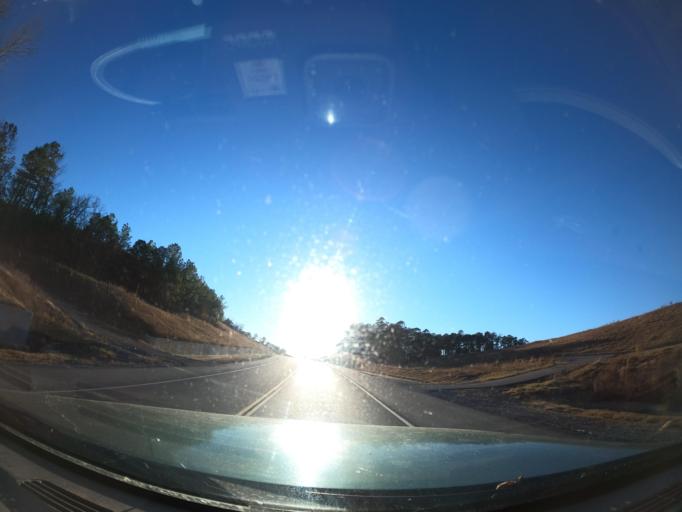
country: US
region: Oklahoma
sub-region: Pittsburg County
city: Hartshorne
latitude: 34.8901
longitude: -95.4576
